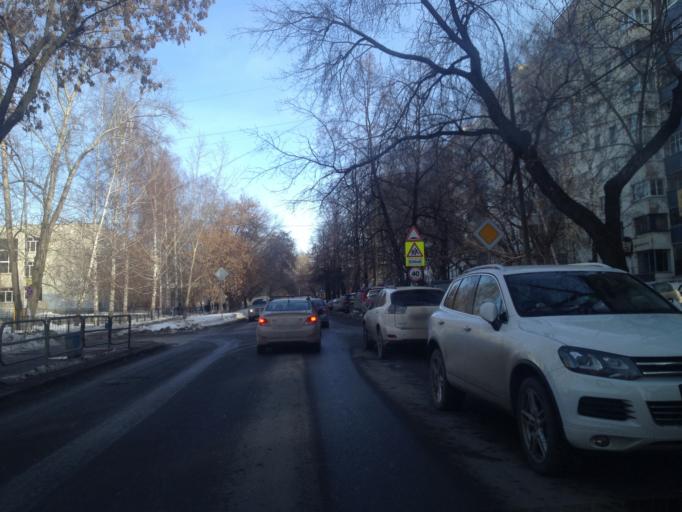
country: RU
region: Sverdlovsk
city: Yekaterinburg
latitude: 56.8320
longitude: 60.6259
